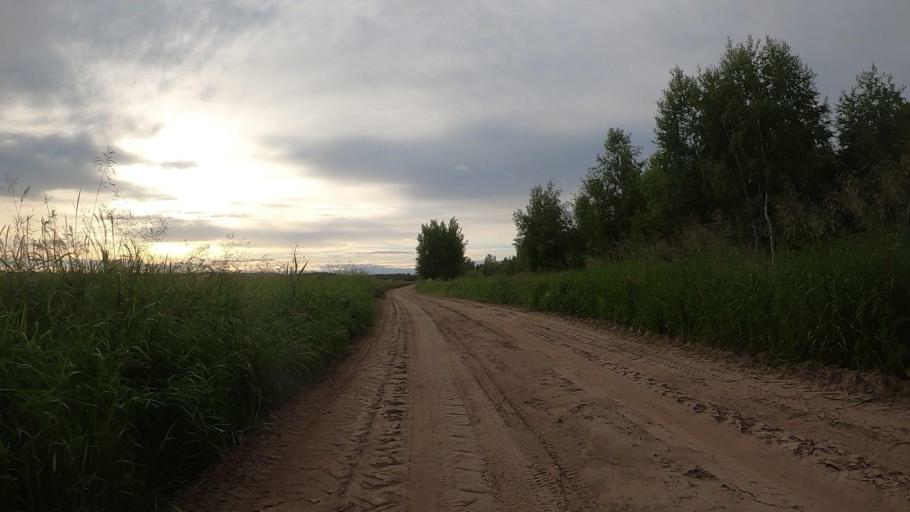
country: LV
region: Olaine
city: Olaine
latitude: 56.8238
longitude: 23.9694
